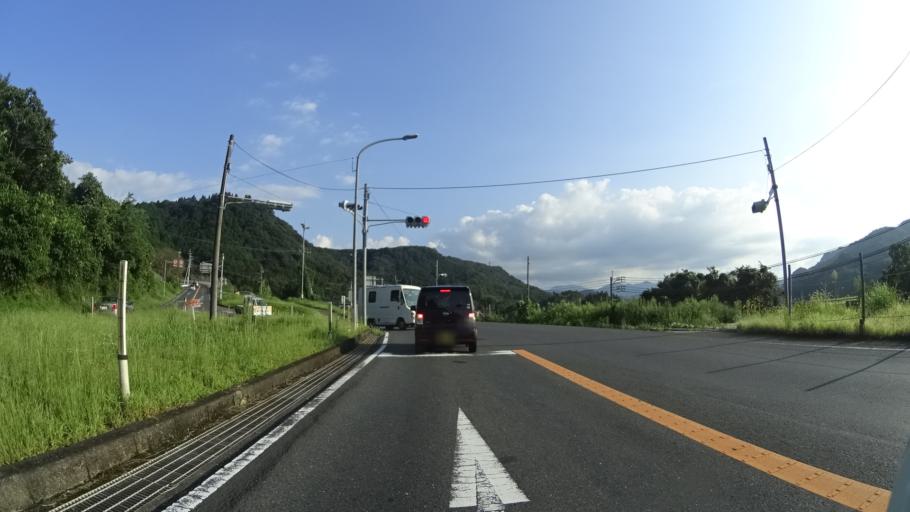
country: JP
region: Oita
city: Bungo-Takada-shi
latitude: 33.4471
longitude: 131.3324
